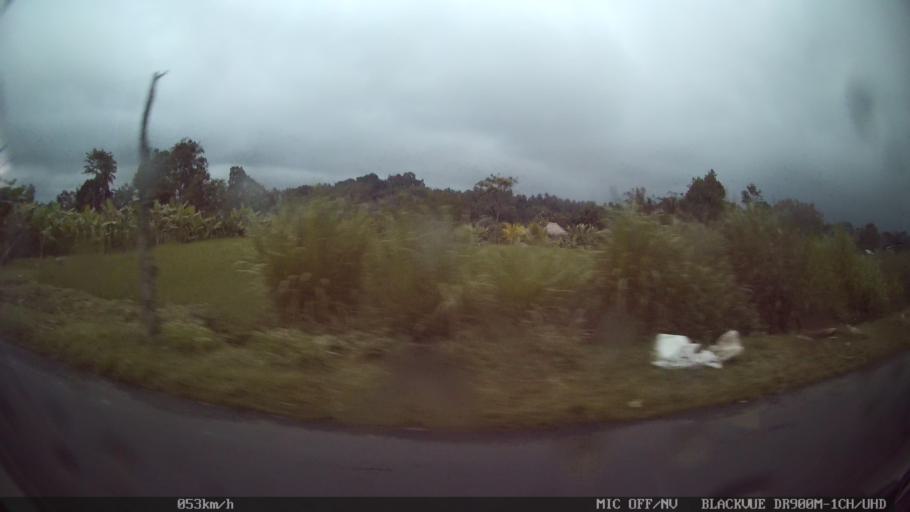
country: ID
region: Bali
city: Banjar Ponggang
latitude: -8.3942
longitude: 115.2550
